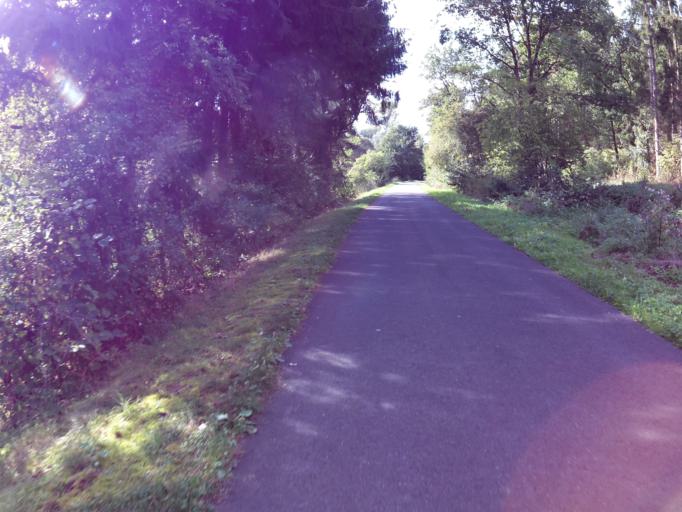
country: DE
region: Rheinland-Pfalz
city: Winterspelt
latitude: 50.2259
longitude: 6.2117
